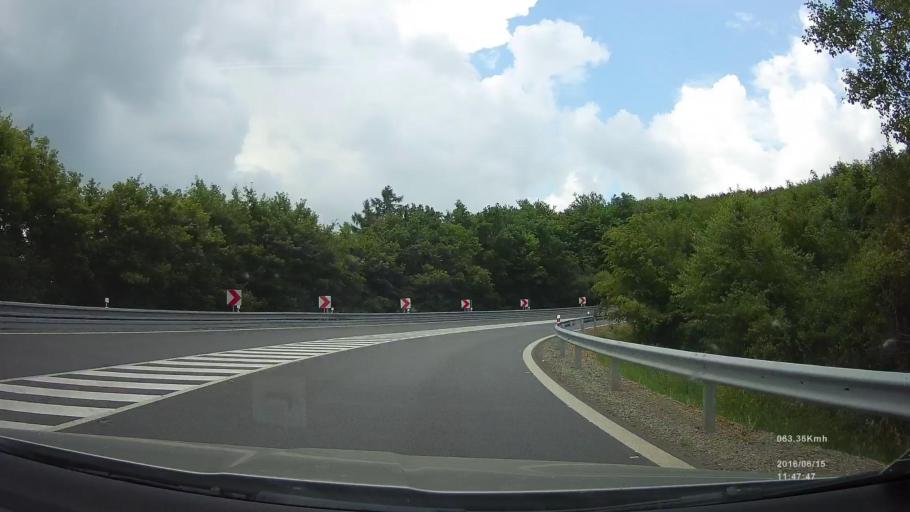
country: SK
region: Kosicky
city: Kosice
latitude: 48.7286
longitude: 21.3262
